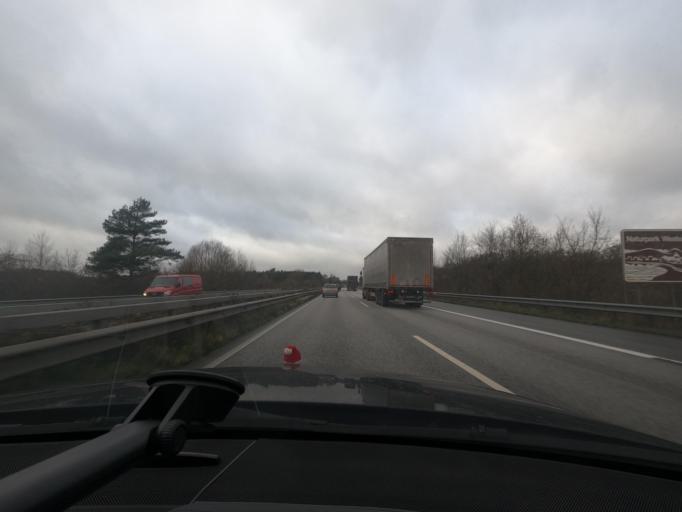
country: DE
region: Schleswig-Holstein
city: Warder
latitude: 54.1953
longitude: 9.8951
